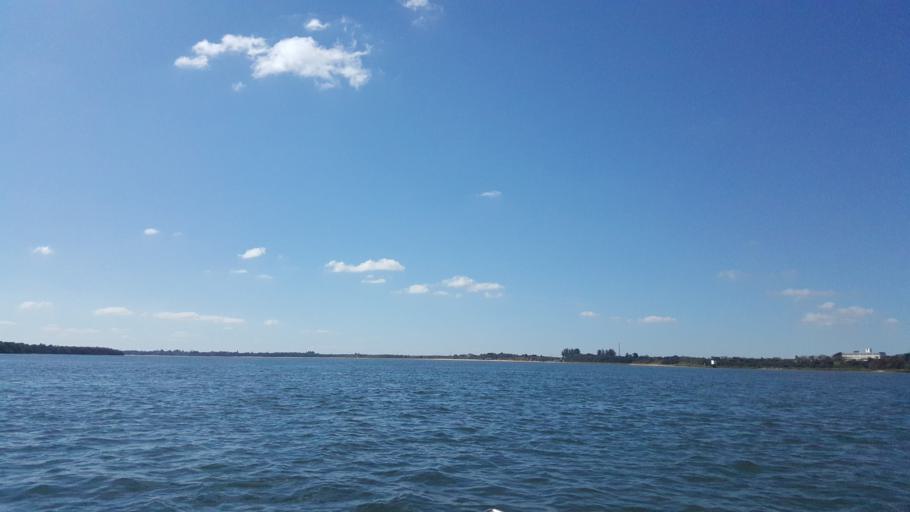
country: AR
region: Corrientes
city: Ituzaingo
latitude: -27.5792
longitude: -56.6913
